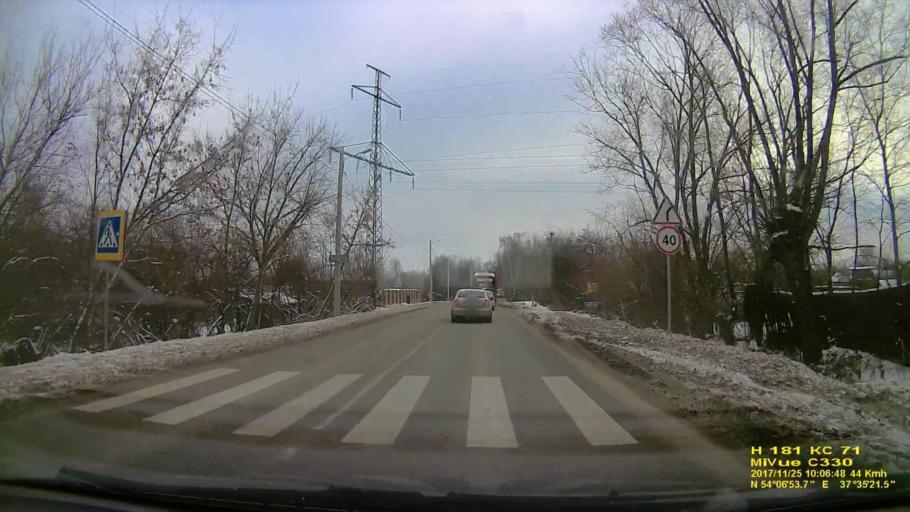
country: RU
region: Tula
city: Skuratovskiy
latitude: 54.1149
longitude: 37.5894
